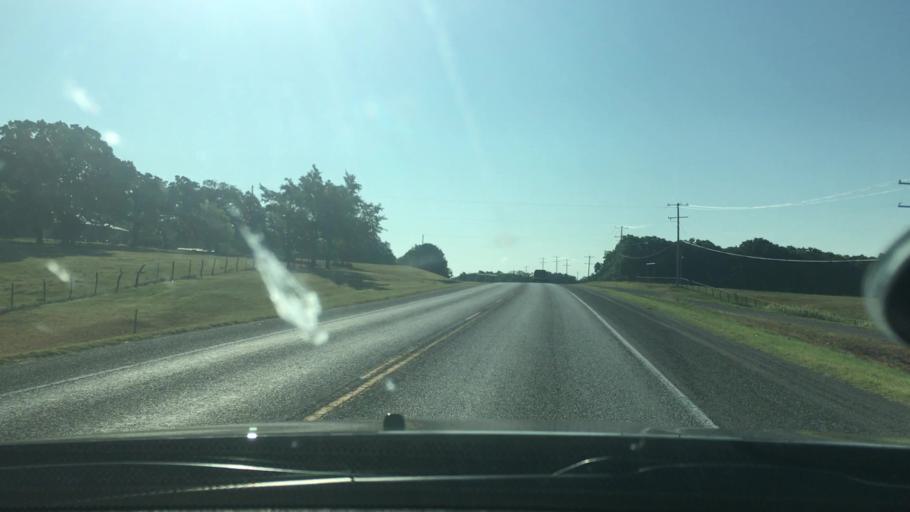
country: US
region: Oklahoma
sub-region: Johnston County
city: Tishomingo
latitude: 34.2381
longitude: -96.7347
